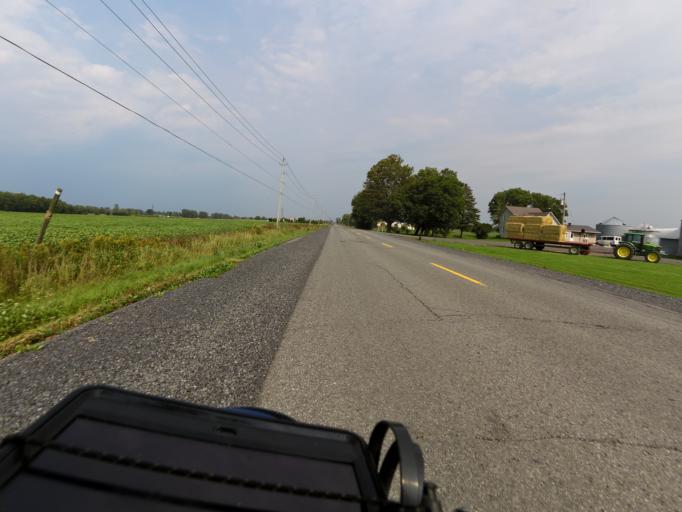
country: CA
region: Ontario
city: Casselman
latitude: 45.1850
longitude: -75.3457
